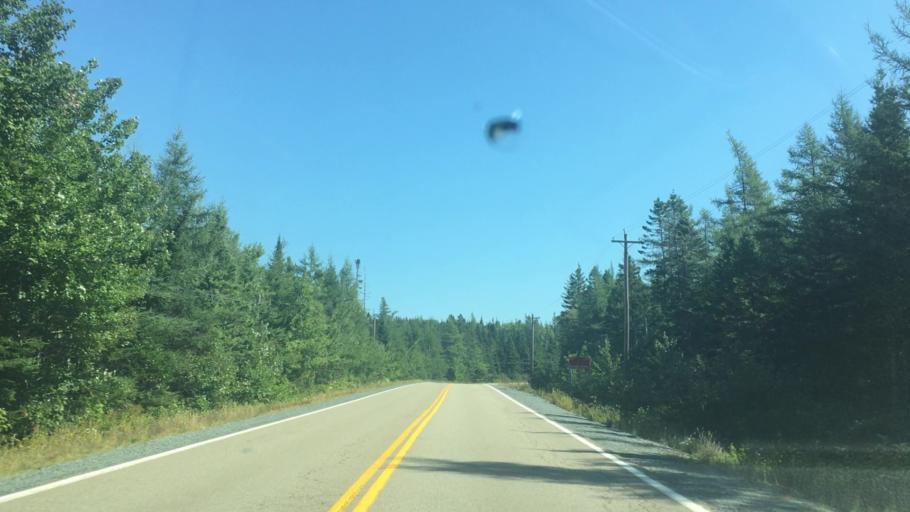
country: CA
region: Nova Scotia
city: Antigonish
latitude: 45.1443
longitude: -61.9978
